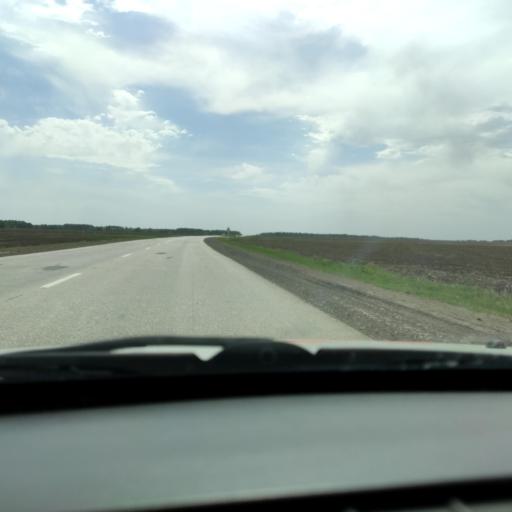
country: RU
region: Samara
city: Yelkhovka
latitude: 53.7219
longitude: 50.2332
